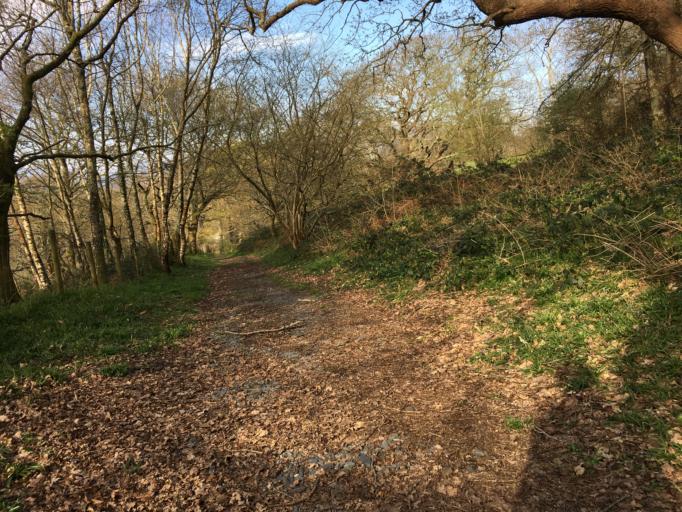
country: GB
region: Wales
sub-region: Gwynedd
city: Porthmadog
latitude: 52.9201
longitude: -4.1047
